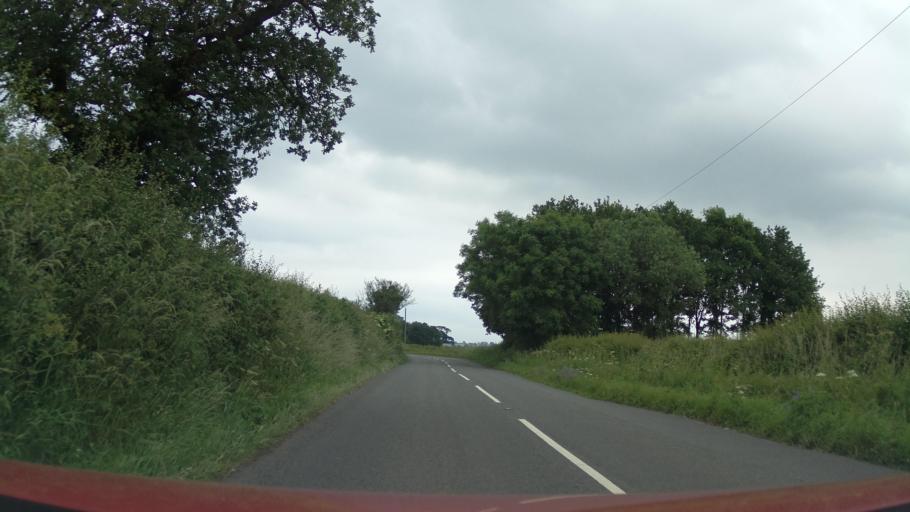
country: GB
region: England
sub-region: Derbyshire
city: Rodsley
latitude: 52.8795
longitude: -1.7475
